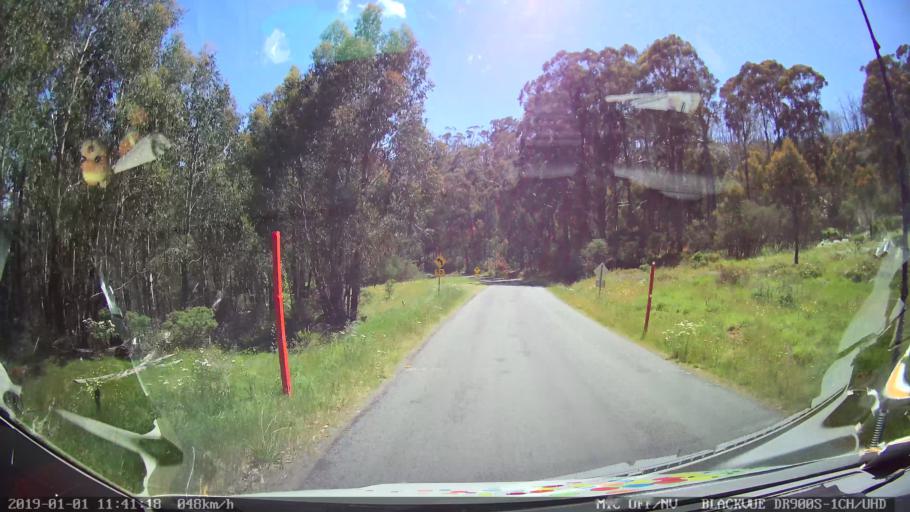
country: AU
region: New South Wales
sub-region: Snowy River
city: Jindabyne
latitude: -35.9150
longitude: 148.3902
